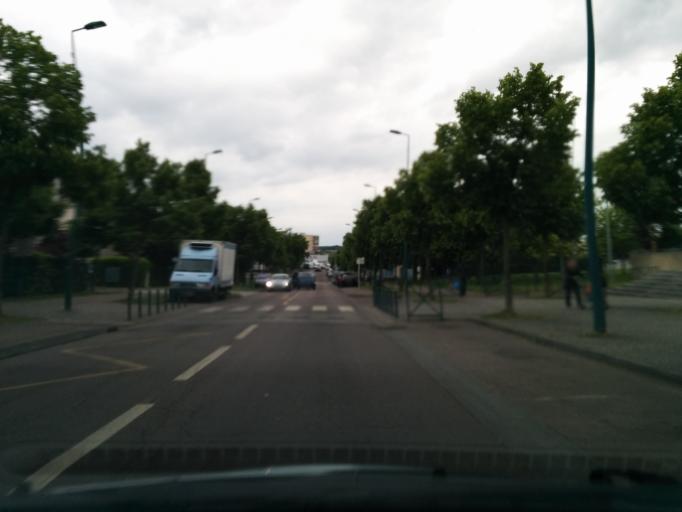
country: FR
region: Ile-de-France
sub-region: Departement des Yvelines
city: Buchelay
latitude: 48.9975
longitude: 1.6882
